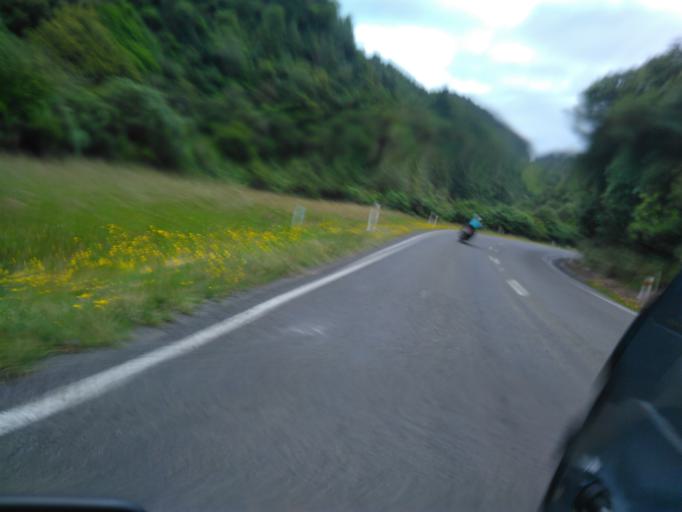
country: NZ
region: Bay of Plenty
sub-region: Opotiki District
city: Opotiki
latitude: -38.3417
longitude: 177.4305
